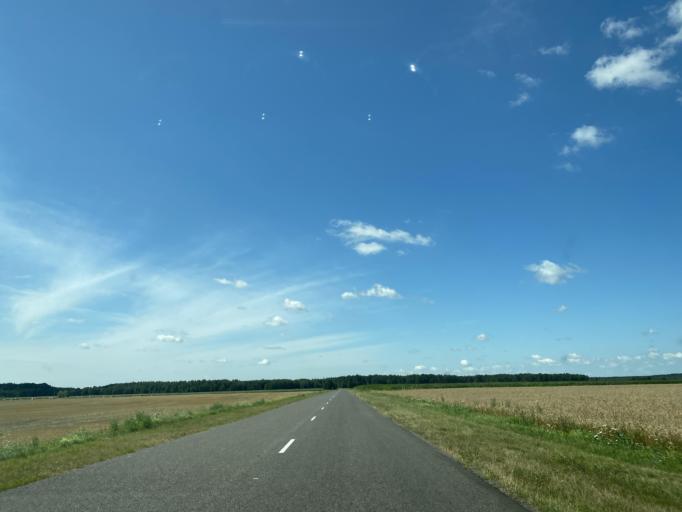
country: BY
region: Brest
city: Ivanava
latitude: 52.2308
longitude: 25.6473
